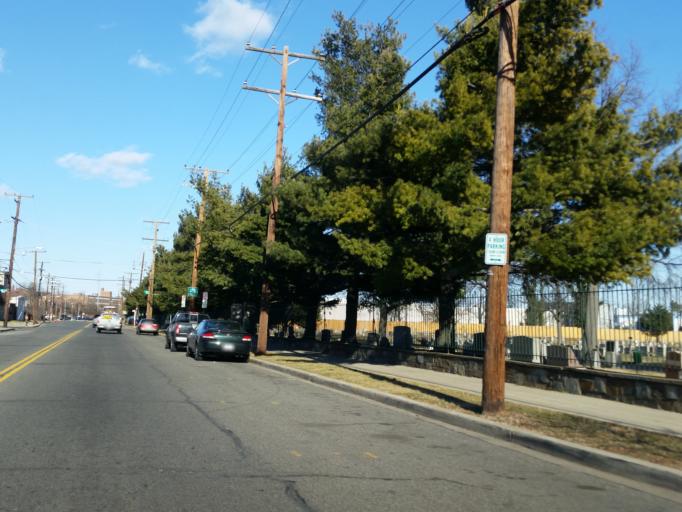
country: US
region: Maryland
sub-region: Prince George's County
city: Mount Rainier
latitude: 38.9147
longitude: -76.9809
